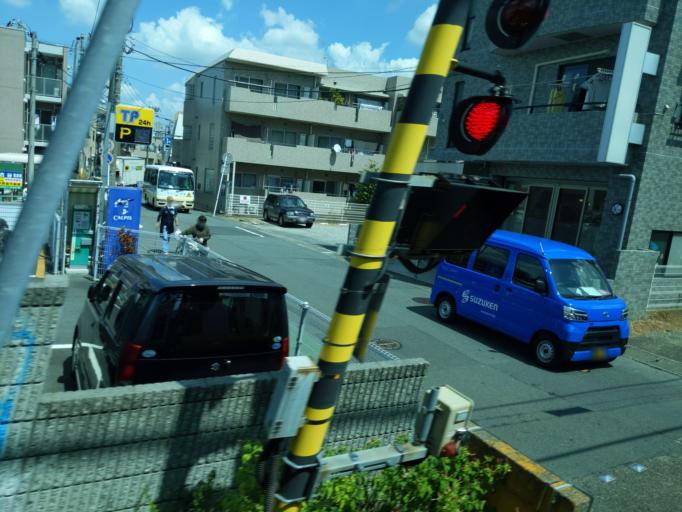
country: JP
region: Tokyo
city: Chofugaoka
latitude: 35.6294
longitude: 139.5538
